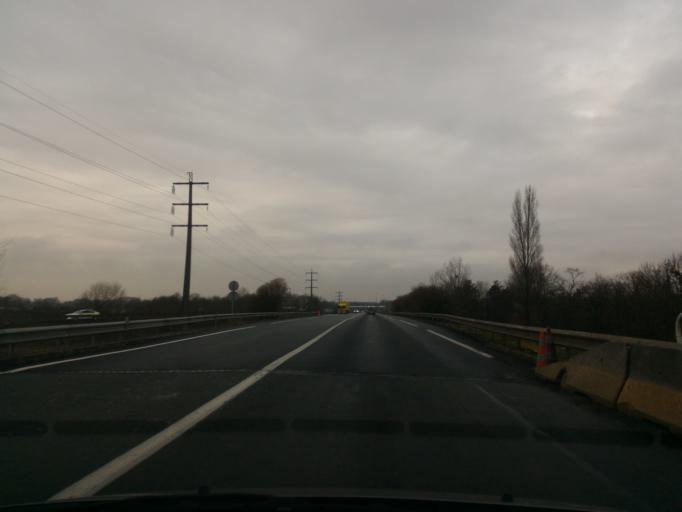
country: FR
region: Poitou-Charentes
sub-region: Departement de la Vienne
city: Biard
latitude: 46.5458
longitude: 0.2966
